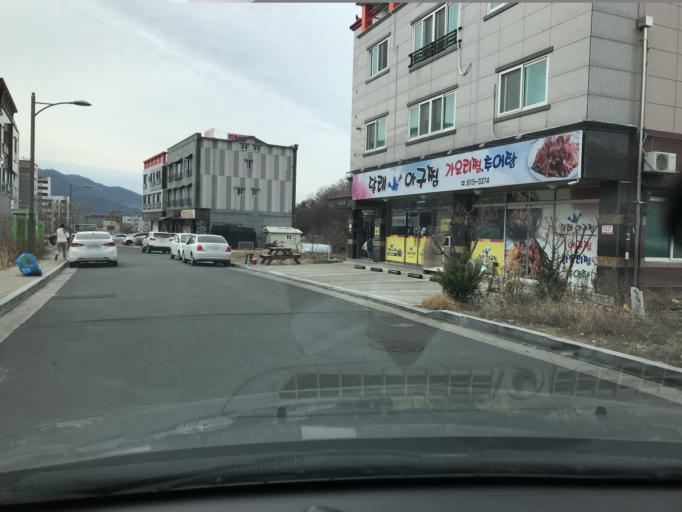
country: KR
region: Daegu
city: Hwawon
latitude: 35.6978
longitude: 128.4540
